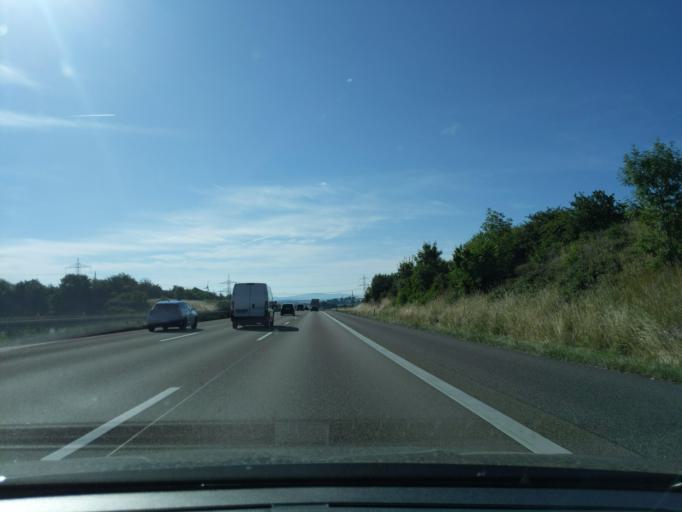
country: DE
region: Hesse
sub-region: Regierungsbezirk Giessen
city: Dehrn
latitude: 50.3727
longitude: 8.1024
